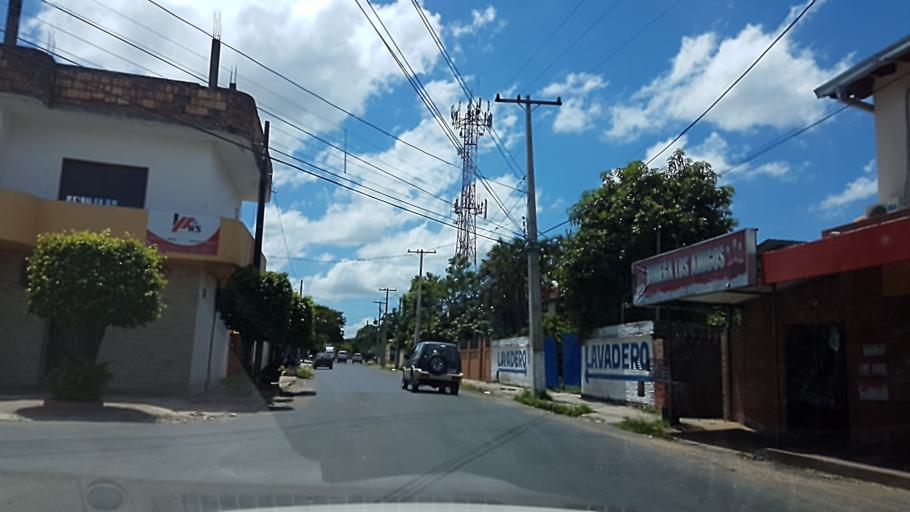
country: PY
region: Central
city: Colonia Mariano Roque Alonso
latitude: -25.2443
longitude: -57.5441
